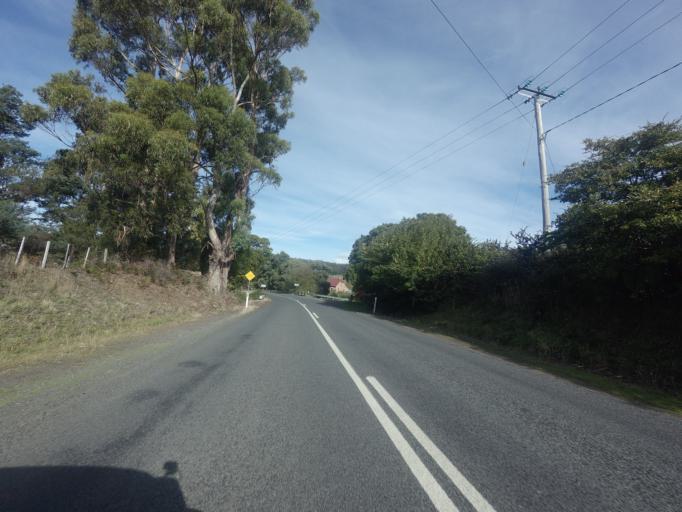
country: AU
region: Tasmania
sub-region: Clarence
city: Sandford
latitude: -43.0613
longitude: 147.8116
